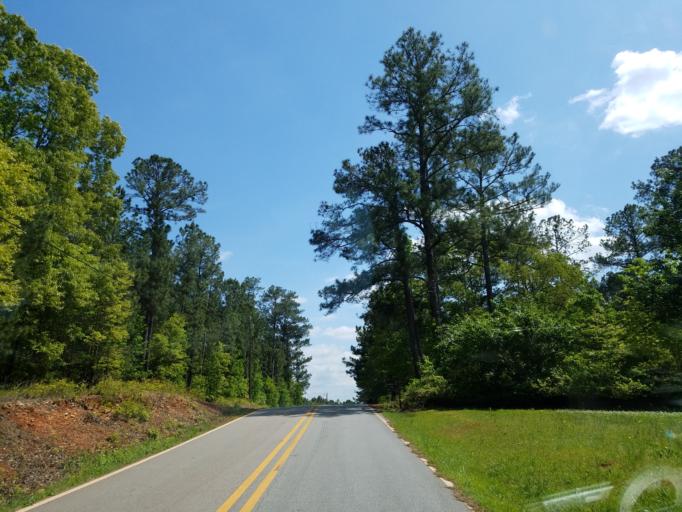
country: US
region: Georgia
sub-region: Butts County
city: Indian Springs
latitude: 33.1676
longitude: -84.0190
